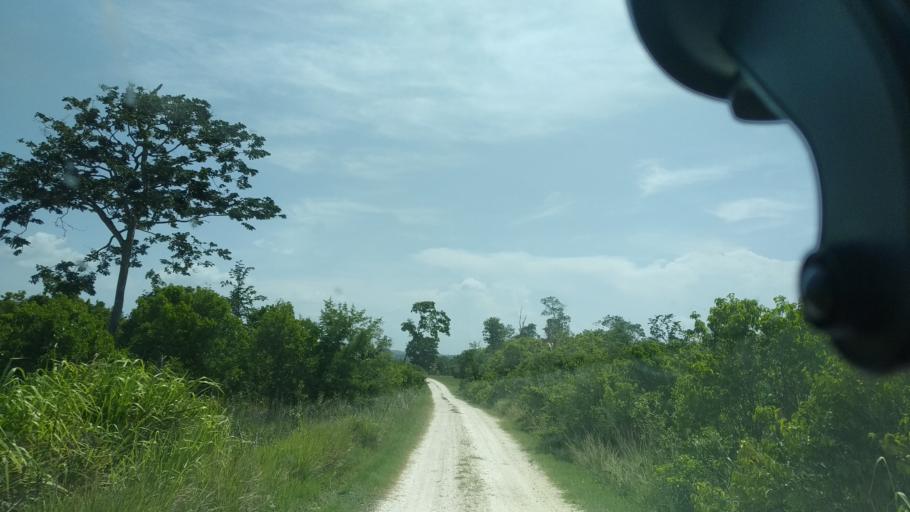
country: BZ
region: Cayo
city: San Ignacio
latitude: 17.2855
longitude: -89.0831
